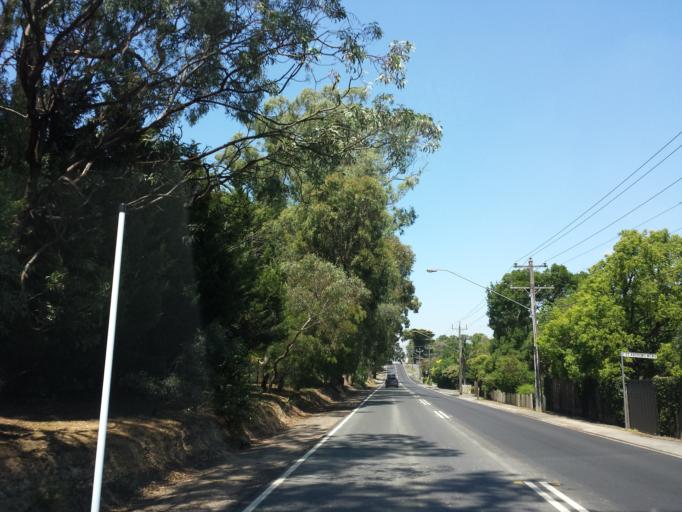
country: AU
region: Victoria
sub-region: Maroondah
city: Croydon North
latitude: -37.7814
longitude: 145.2934
